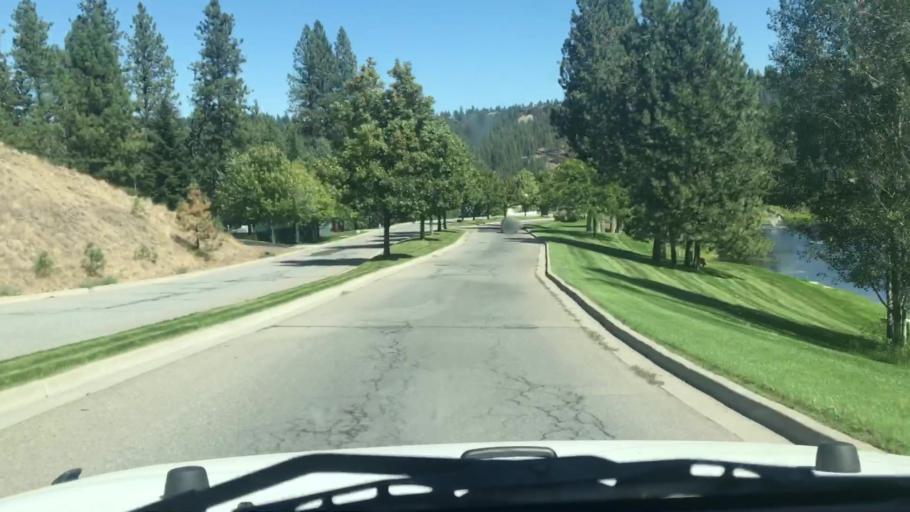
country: US
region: Washington
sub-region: Spokane County
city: Spokane
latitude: 47.5972
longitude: -117.4154
